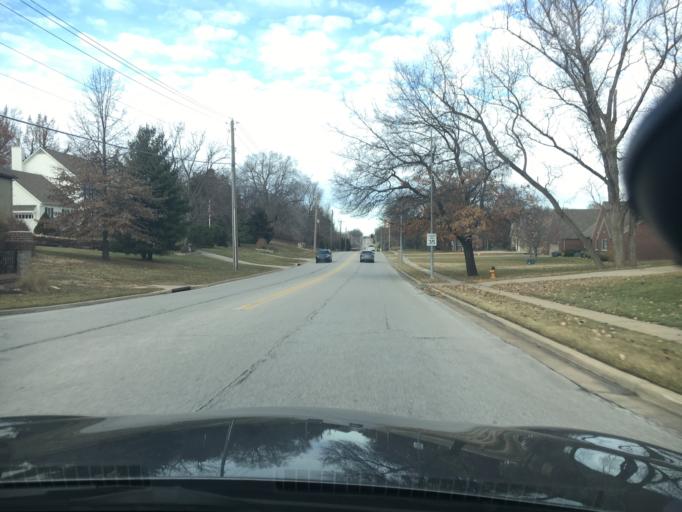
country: US
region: Kansas
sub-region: Johnson County
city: Leawood
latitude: 38.9026
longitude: -94.6305
